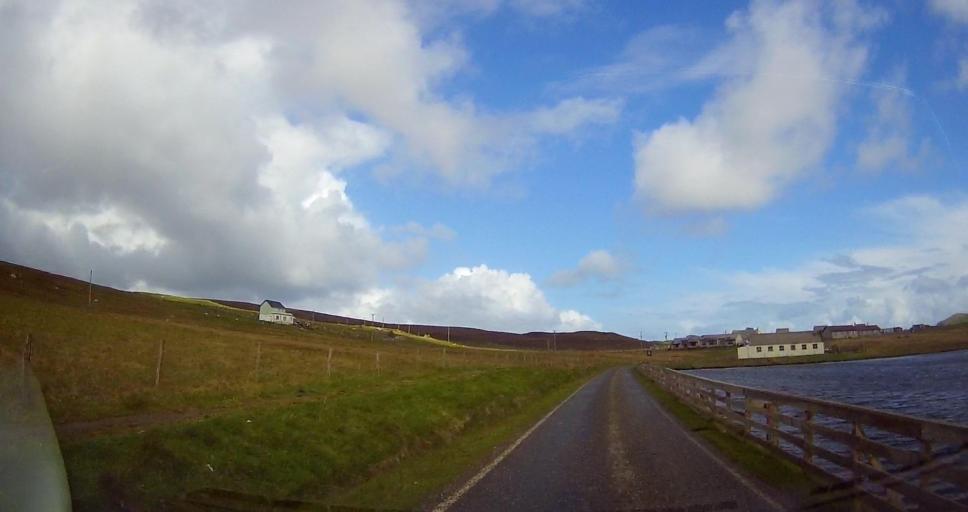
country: GB
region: Scotland
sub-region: Shetland Islands
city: Lerwick
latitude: 60.5835
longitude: -1.3363
